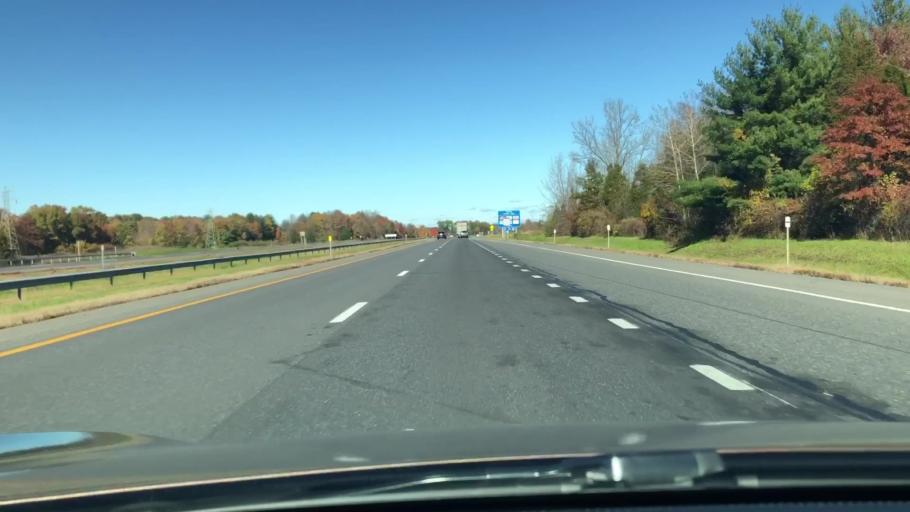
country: US
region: New York
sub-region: Ulster County
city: Saugerties South
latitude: 42.0580
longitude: -73.9825
